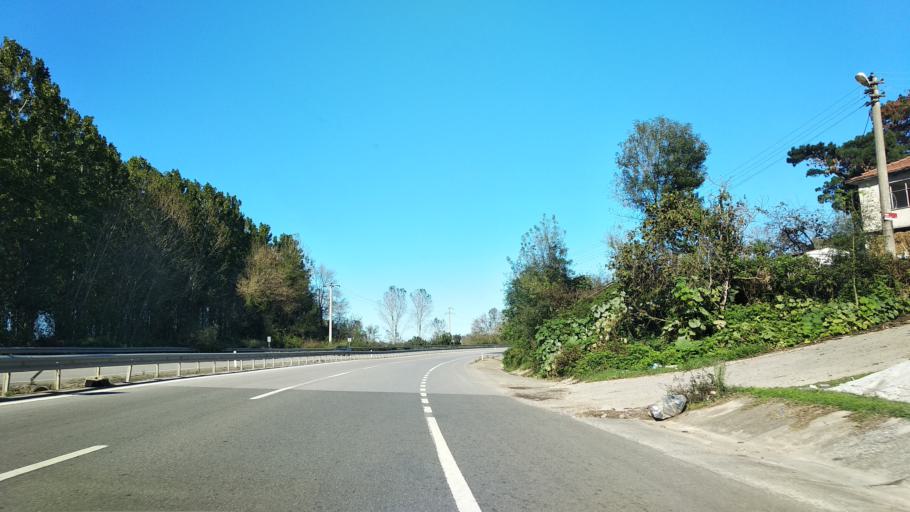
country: TR
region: Sakarya
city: Karasu
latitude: 41.0889
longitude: 30.6474
